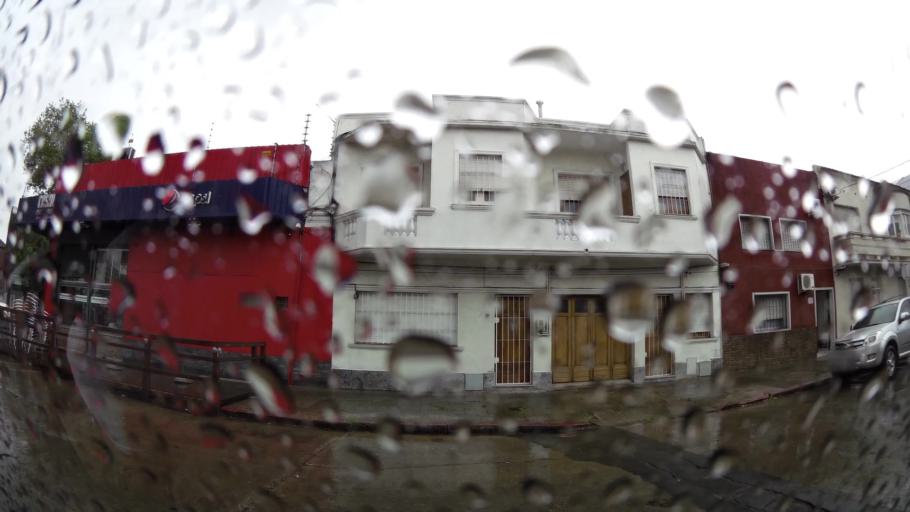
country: UY
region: Montevideo
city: Montevideo
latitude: -34.8753
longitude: -56.1782
